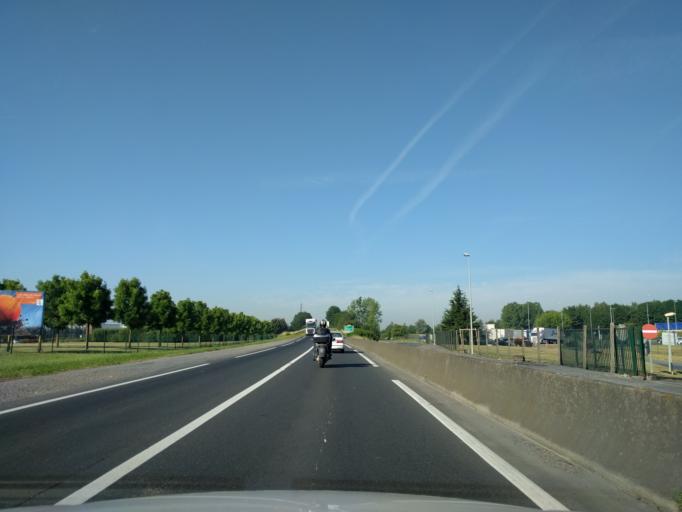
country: FR
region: Picardie
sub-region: Departement de la Somme
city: Roye
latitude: 49.6815
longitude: 2.7761
